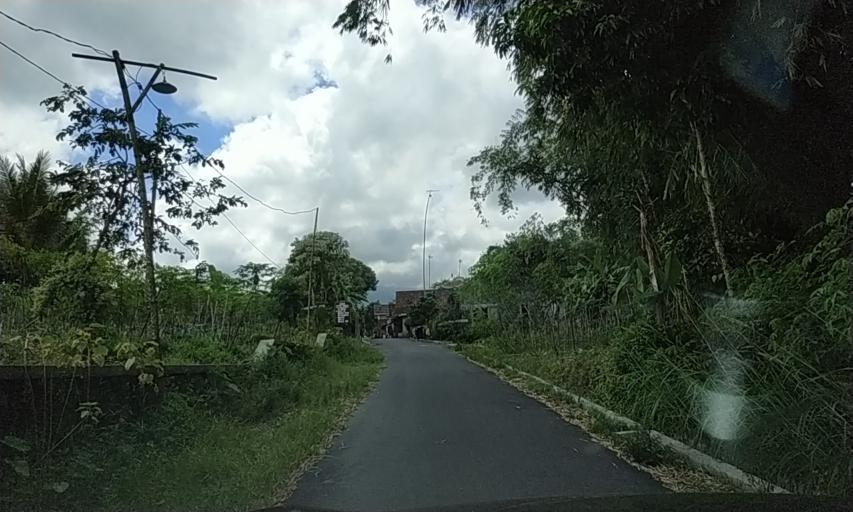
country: ID
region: Central Java
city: Muntilan
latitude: -7.5395
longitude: 110.3559
